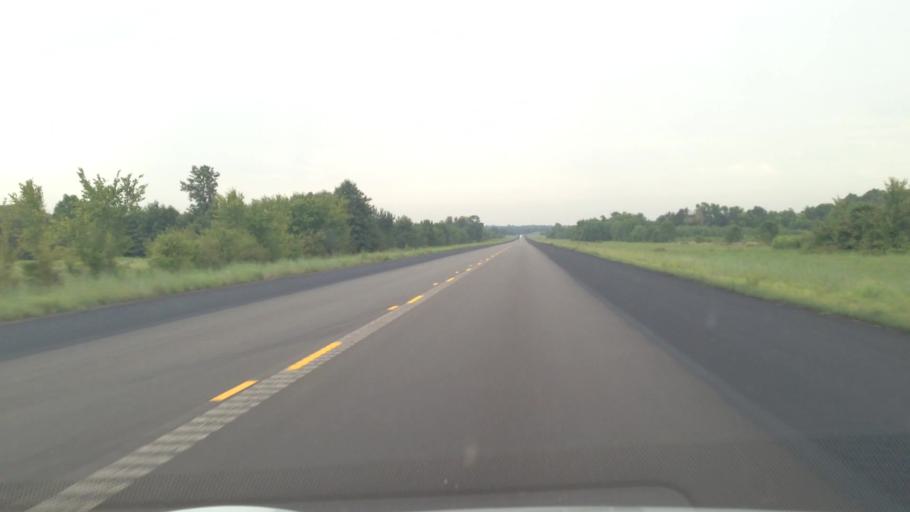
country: US
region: Kansas
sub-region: Cherokee County
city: Baxter Springs
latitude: 37.0432
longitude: -94.7113
